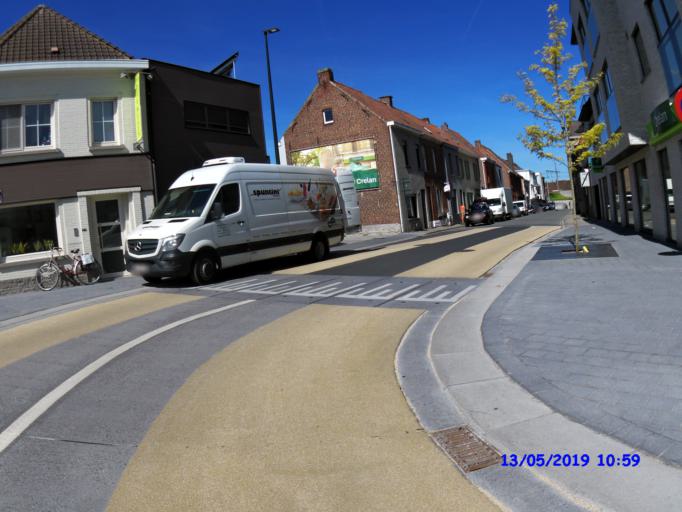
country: BE
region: Flanders
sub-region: Provincie West-Vlaanderen
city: Waregem
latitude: 50.8886
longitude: 3.4223
